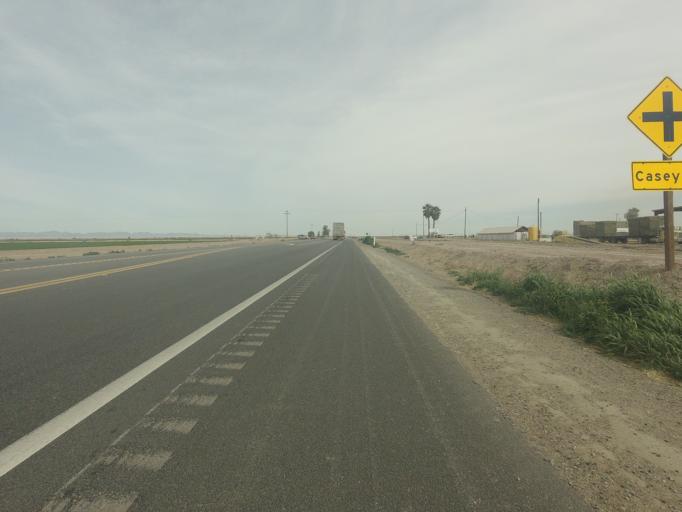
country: US
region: California
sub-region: Imperial County
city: Brawley
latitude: 32.9744
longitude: -115.4253
